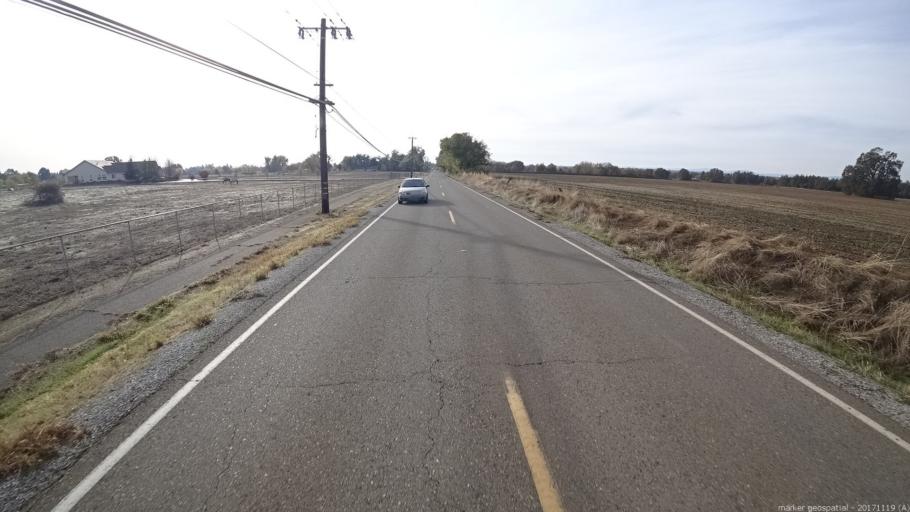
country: US
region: California
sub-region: Shasta County
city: Anderson
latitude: 40.5124
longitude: -122.3336
